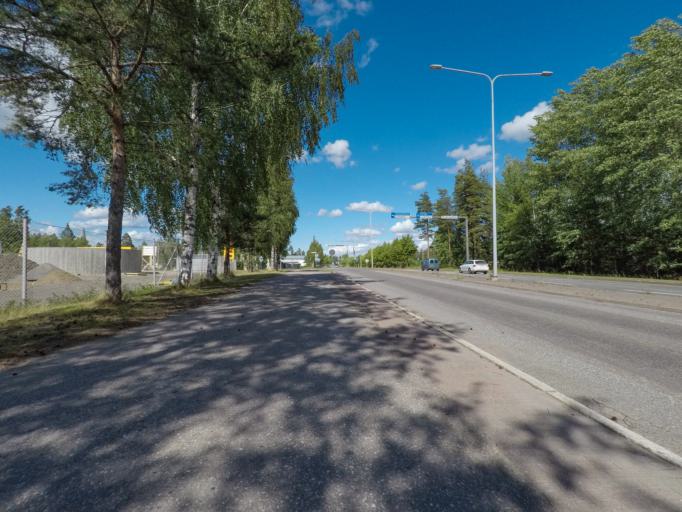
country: FI
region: South Karelia
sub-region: Lappeenranta
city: Lappeenranta
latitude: 61.0655
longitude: 28.2564
